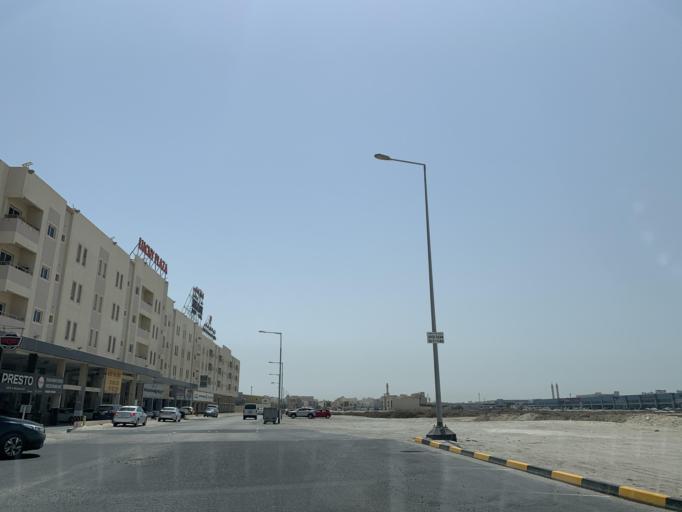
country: BH
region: Northern
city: Madinat `Isa
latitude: 26.1952
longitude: 50.5435
